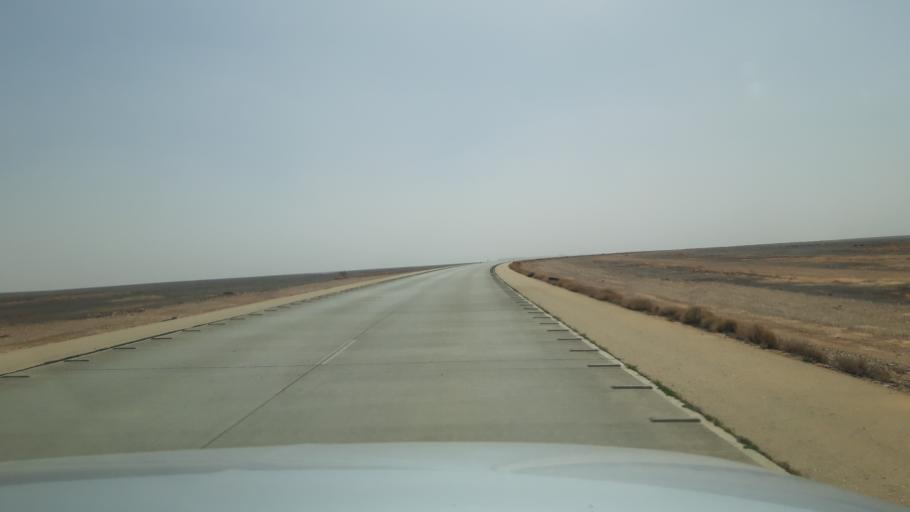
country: JO
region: Ma'an
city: Al Jafr
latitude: 30.9615
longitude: 36.6230
